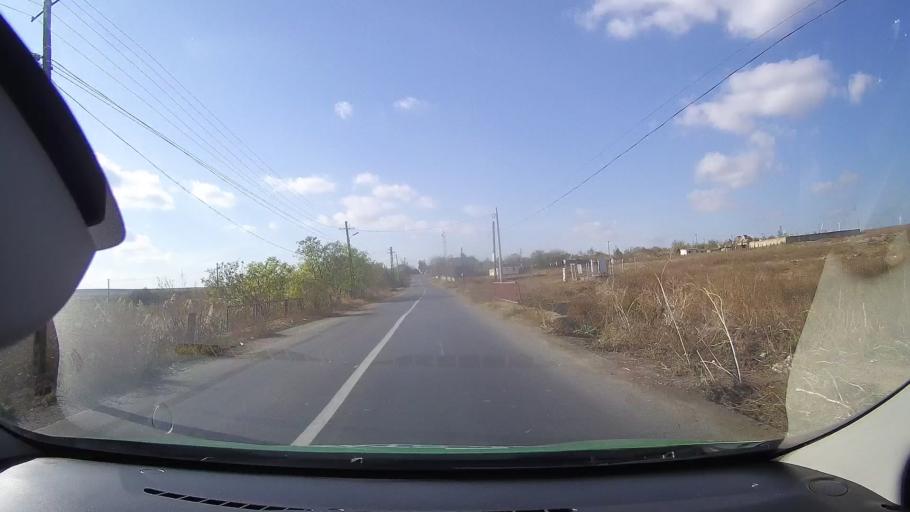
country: RO
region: Constanta
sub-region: Comuna Cogealac
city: Tariverde
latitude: 44.5627
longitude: 28.5962
